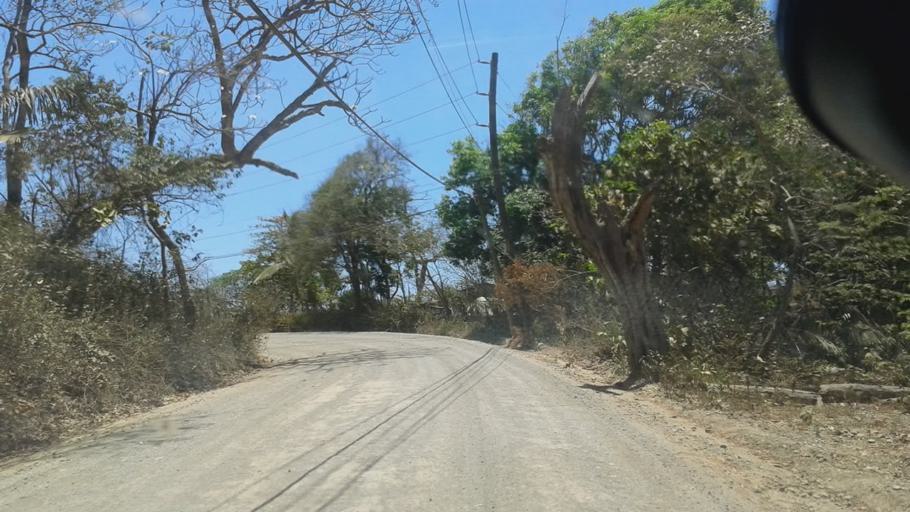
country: CR
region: Guanacaste
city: Samara
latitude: 10.0117
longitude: -85.7182
